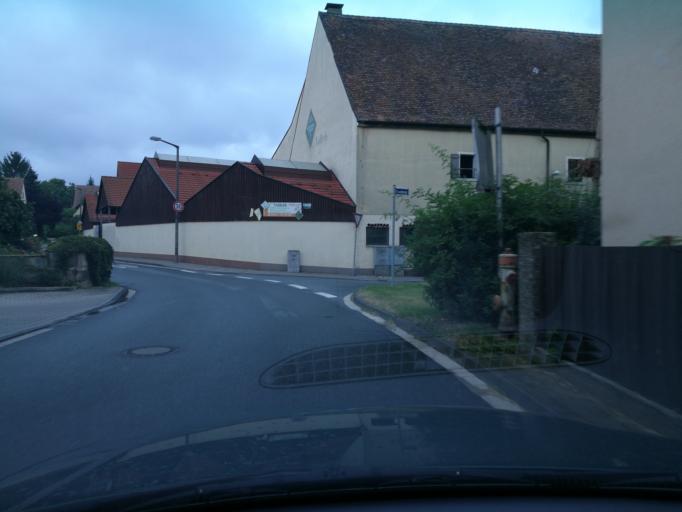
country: DE
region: Bavaria
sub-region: Regierungsbezirk Mittelfranken
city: Obermichelbach
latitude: 49.5396
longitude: 10.9600
